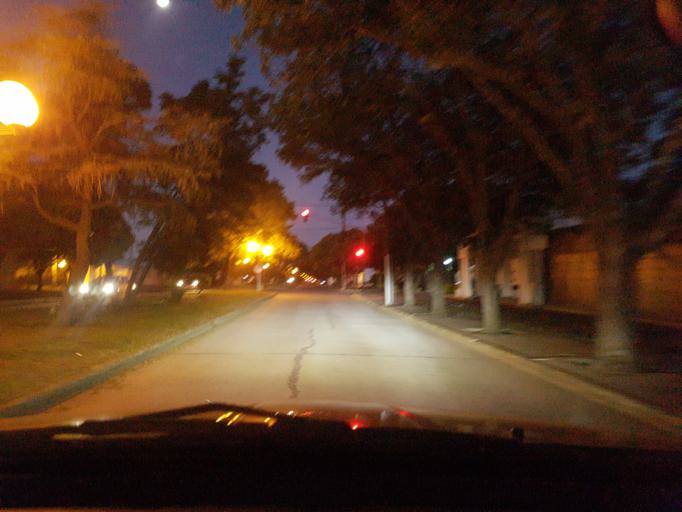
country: AR
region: Cordoba
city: General Cabrera
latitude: -32.7608
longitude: -63.7882
